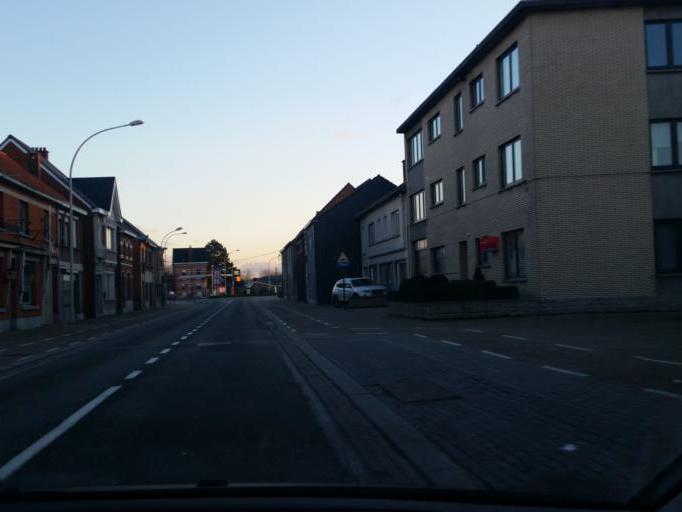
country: BE
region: Flanders
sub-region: Provincie Oost-Vlaanderen
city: Sint-Gillis-Waas
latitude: 51.2554
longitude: 4.1889
